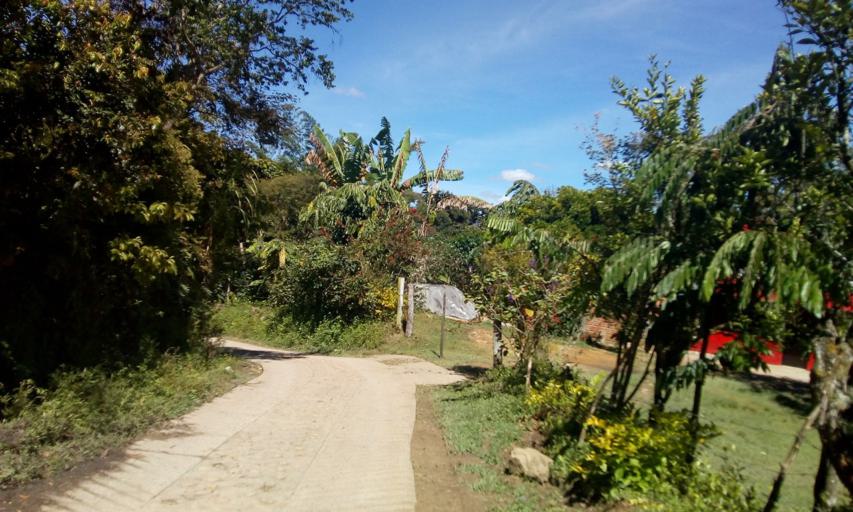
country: CO
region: Santander
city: Guepsa
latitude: 6.0003
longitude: -73.5578
